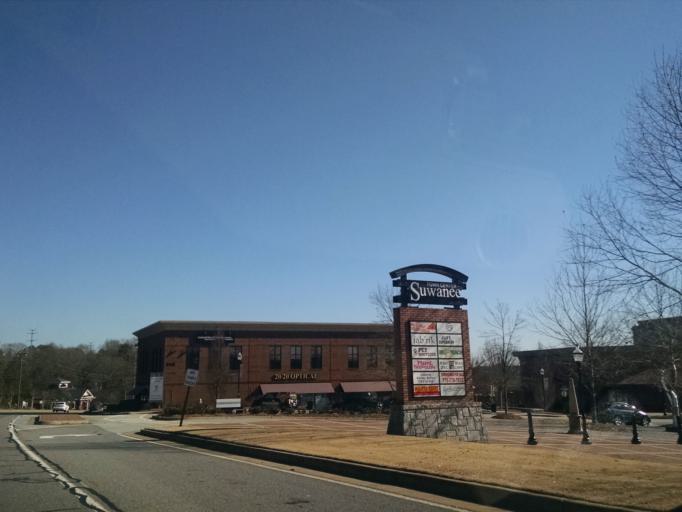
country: US
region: Georgia
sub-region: Gwinnett County
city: Suwanee
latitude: 34.0570
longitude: -84.0632
